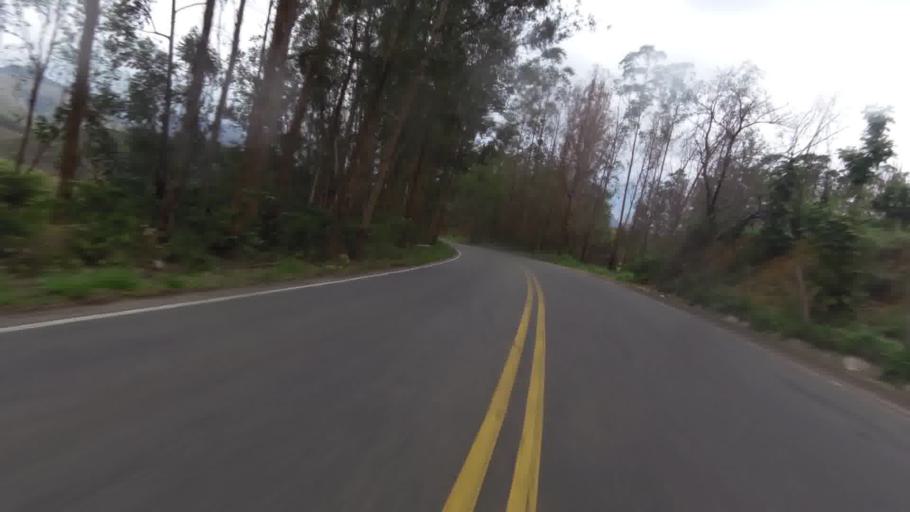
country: BR
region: Espirito Santo
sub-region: Alfredo Chaves
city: Alfredo Chaves
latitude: -20.6663
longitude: -40.7204
